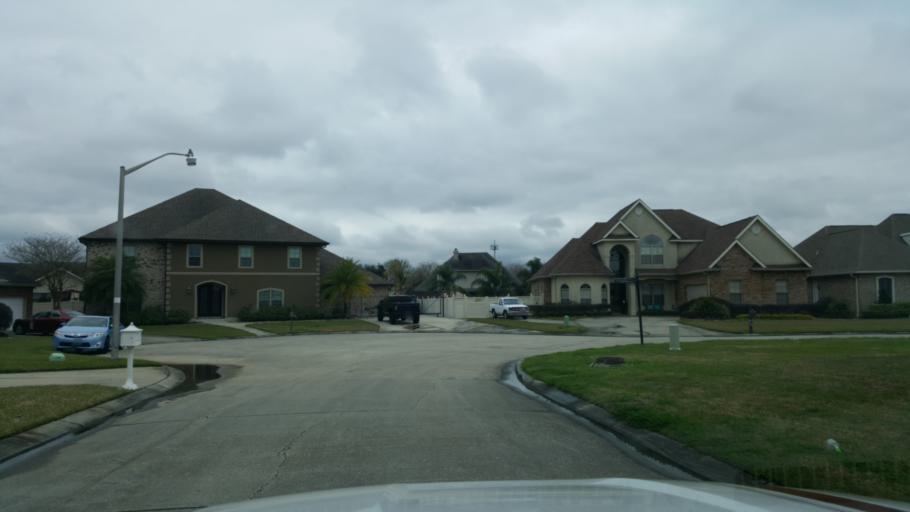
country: US
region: Louisiana
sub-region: Jefferson Parish
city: Woodmere
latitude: 29.8790
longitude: -90.0806
